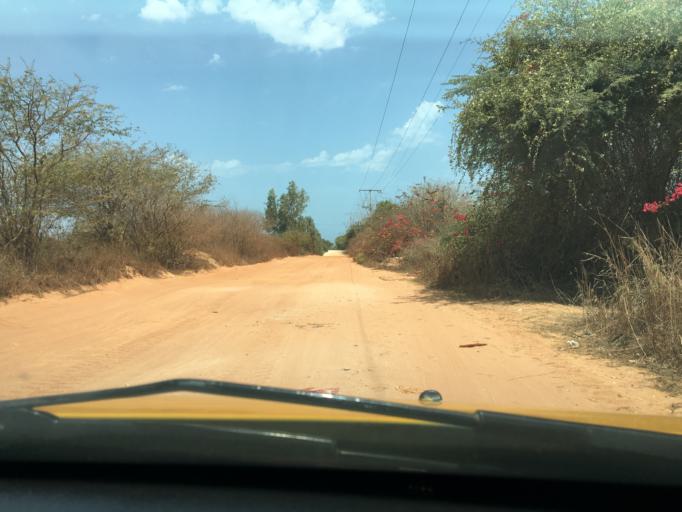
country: SN
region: Thies
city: Thies
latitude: 14.8193
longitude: -17.1999
